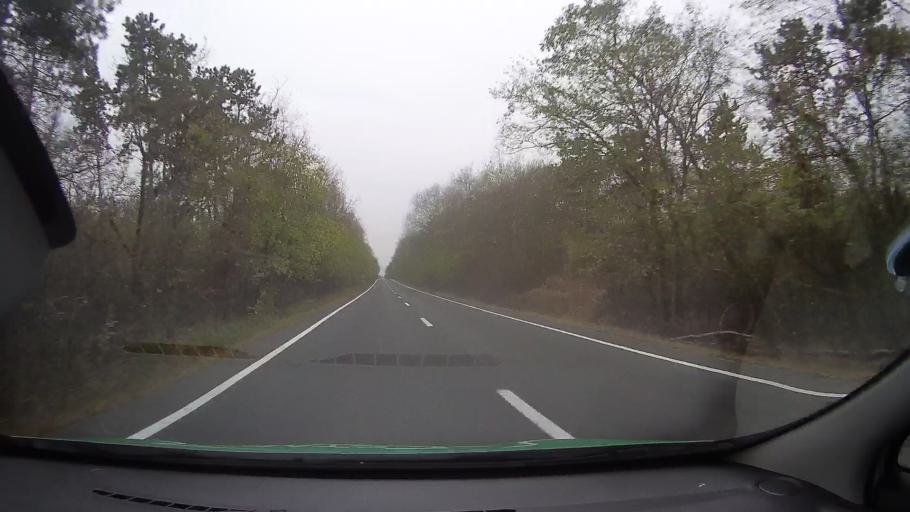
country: RO
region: Ialomita
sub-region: Comuna Mihail Kogalniceanu
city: Mihail Kogalniceanu
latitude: 44.6758
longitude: 27.7647
